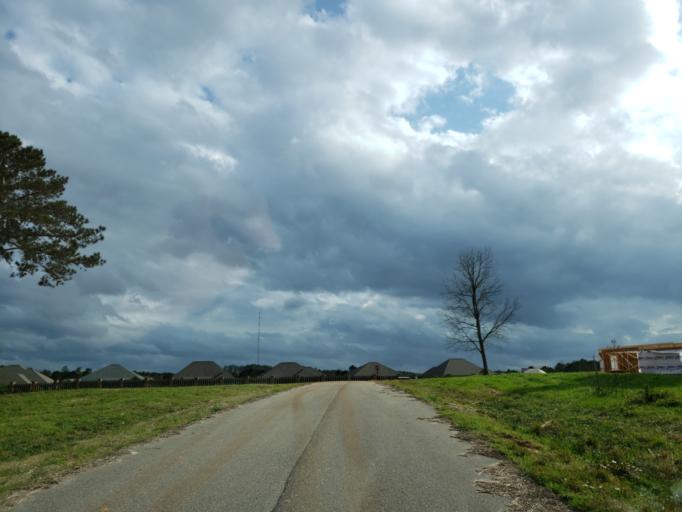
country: US
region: Mississippi
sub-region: Jones County
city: Ellisville
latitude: 31.5590
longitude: -89.2557
